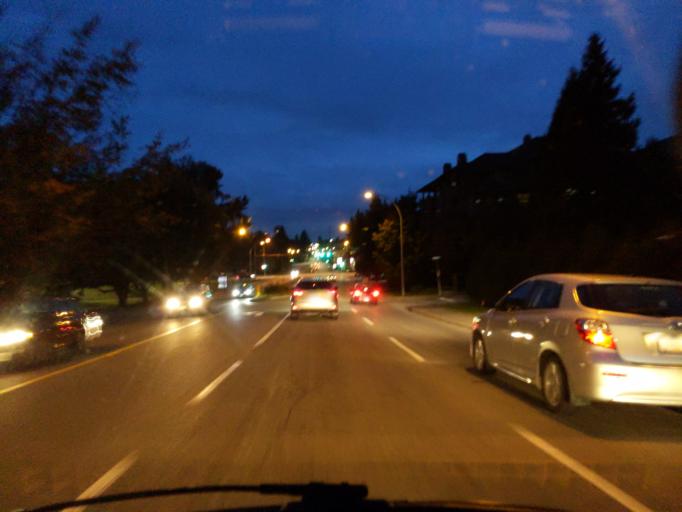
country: CA
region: British Columbia
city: New Westminster
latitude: 49.2234
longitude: -122.9102
